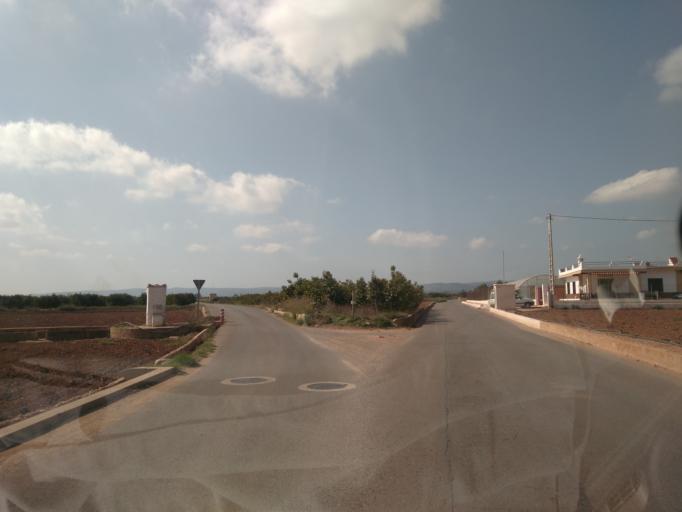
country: ES
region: Valencia
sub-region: Provincia de Valencia
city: L'Alcudia
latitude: 39.1894
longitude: -0.5252
